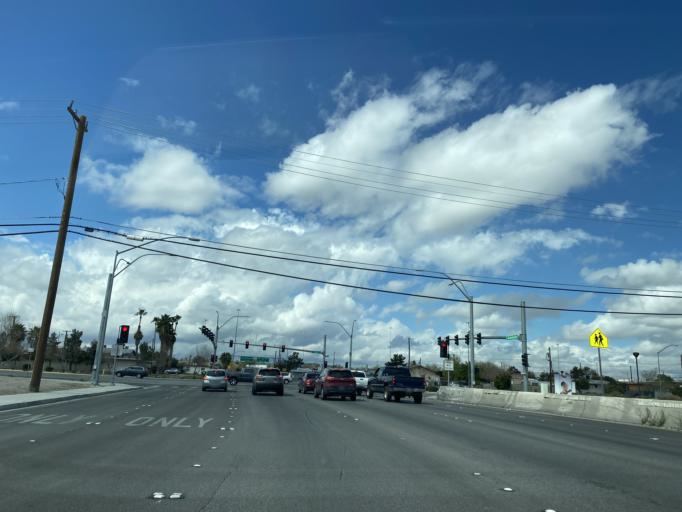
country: US
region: Nevada
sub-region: Clark County
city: North Las Vegas
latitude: 36.1969
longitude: -115.1332
